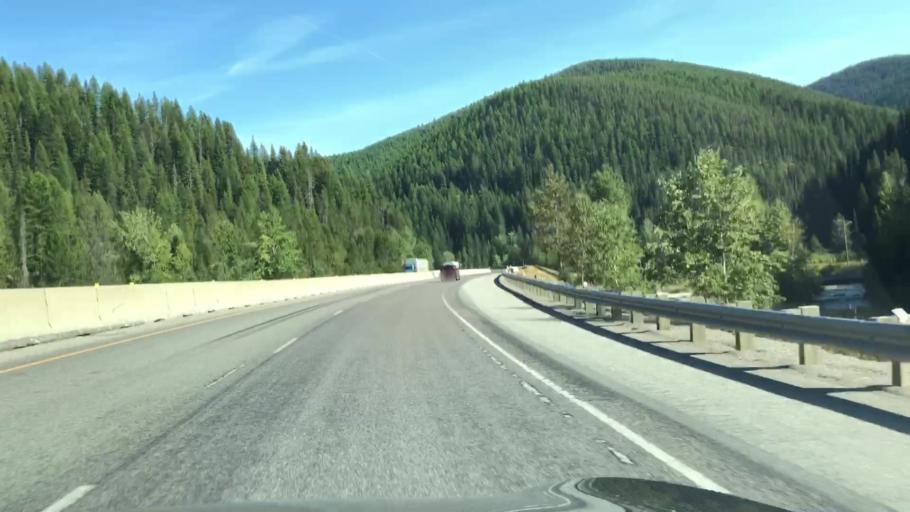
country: US
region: Montana
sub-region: Sanders County
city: Thompson Falls
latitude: 47.4184
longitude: -115.5918
